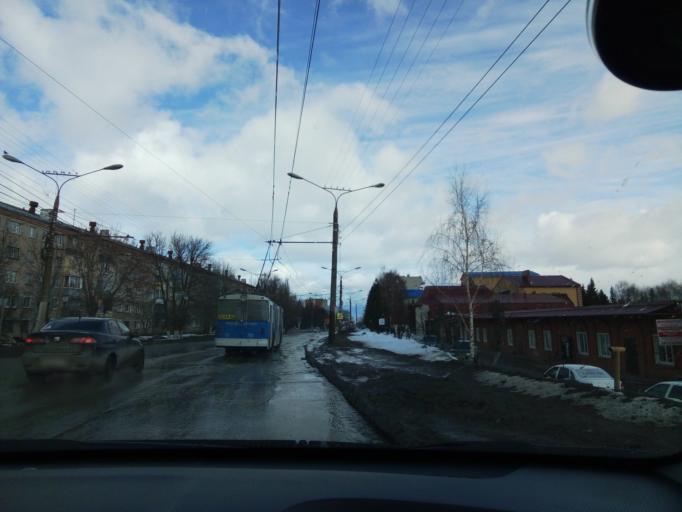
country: RU
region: Chuvashia
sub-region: Cheboksarskiy Rayon
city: Cheboksary
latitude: 56.1229
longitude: 47.2016
